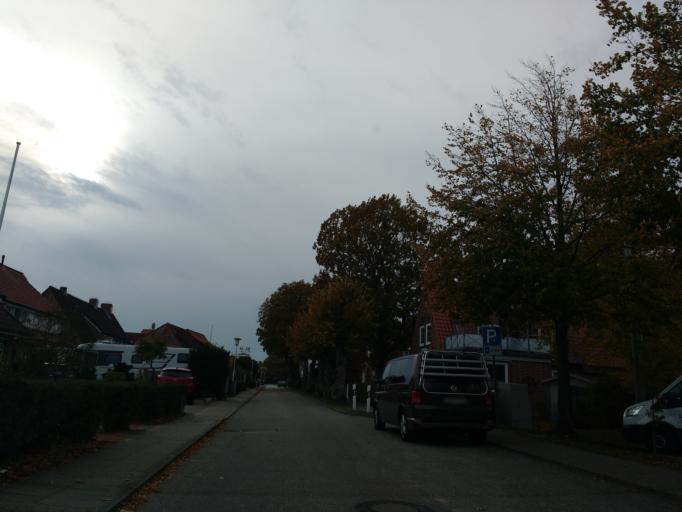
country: DE
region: Schleswig-Holstein
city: Gromitz
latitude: 54.1484
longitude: 10.9676
